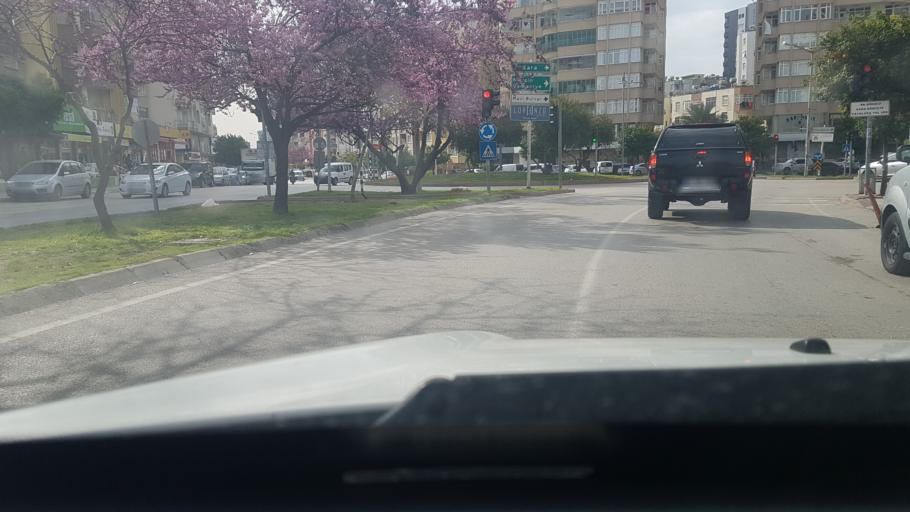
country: TR
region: Adana
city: Adana
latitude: 37.0400
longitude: 35.3025
